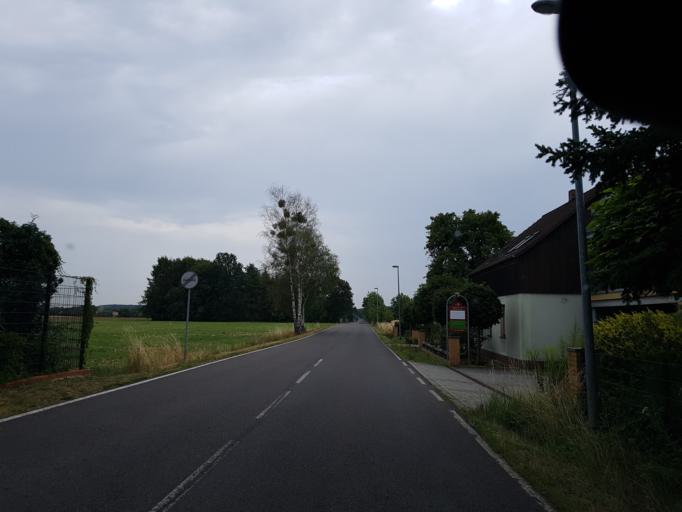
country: DE
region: Brandenburg
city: Schipkau
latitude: 51.5532
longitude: 13.9171
